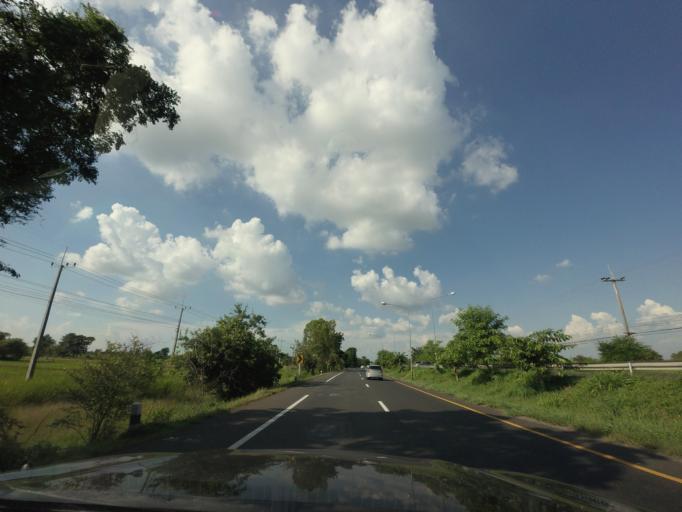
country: TH
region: Nakhon Ratchasima
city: Bua Lai
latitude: 15.6836
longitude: 102.5776
